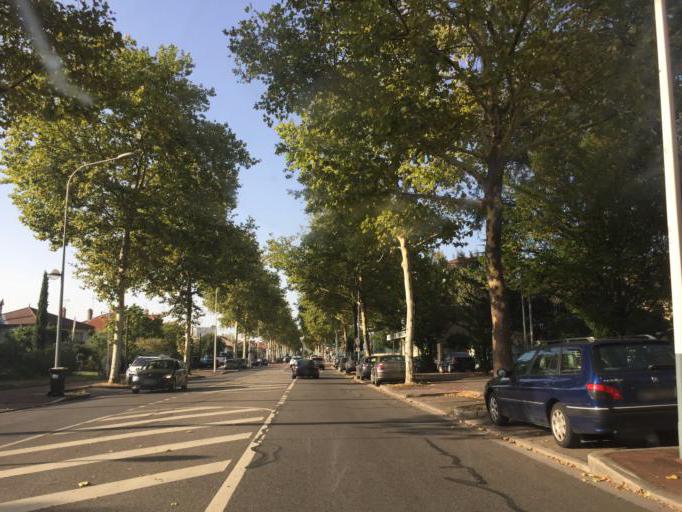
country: FR
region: Rhone-Alpes
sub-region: Departement du Rhone
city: Venissieux
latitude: 45.7250
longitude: 4.8871
